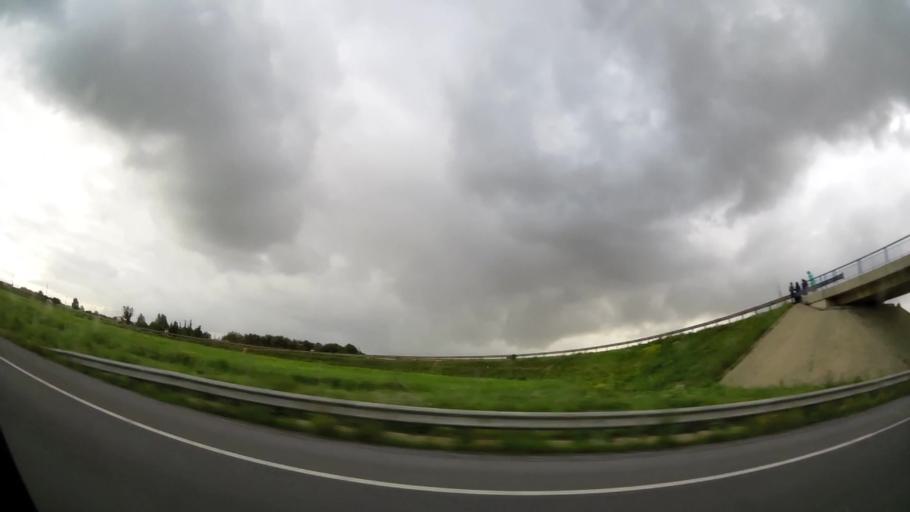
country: MA
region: Grand Casablanca
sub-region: Mediouna
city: Tit Mellil
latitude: 33.5860
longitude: -7.4519
